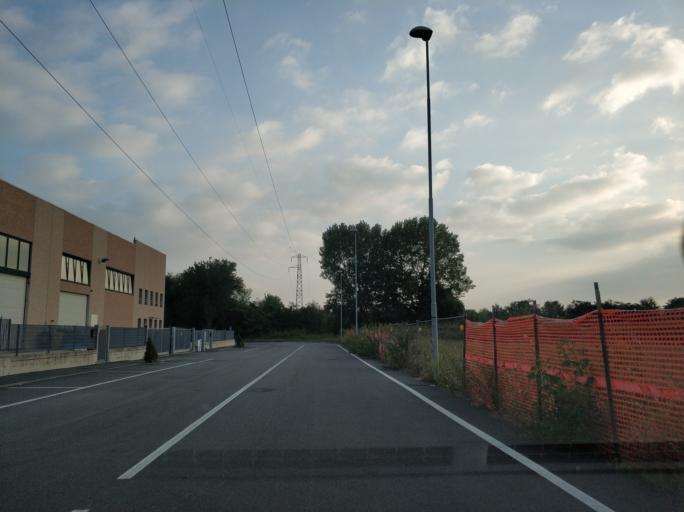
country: IT
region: Piedmont
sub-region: Provincia di Torino
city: San Maurizio
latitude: 45.2198
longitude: 7.6411
